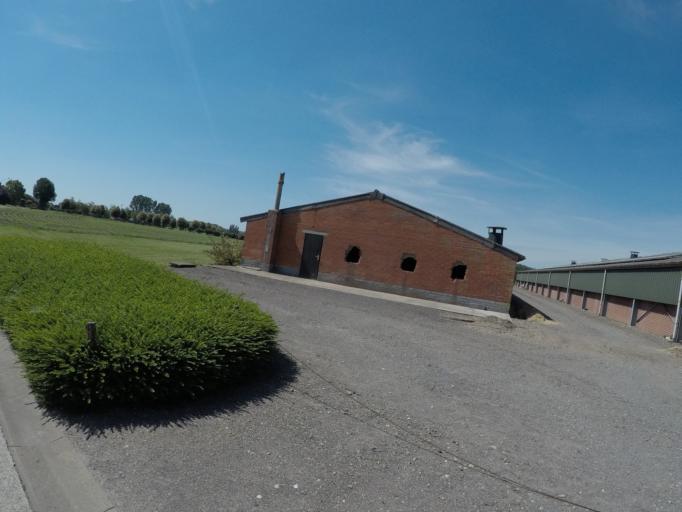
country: NL
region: North Brabant
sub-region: Gemeente Zundert
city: Zundert
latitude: 51.4127
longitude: 4.6614
